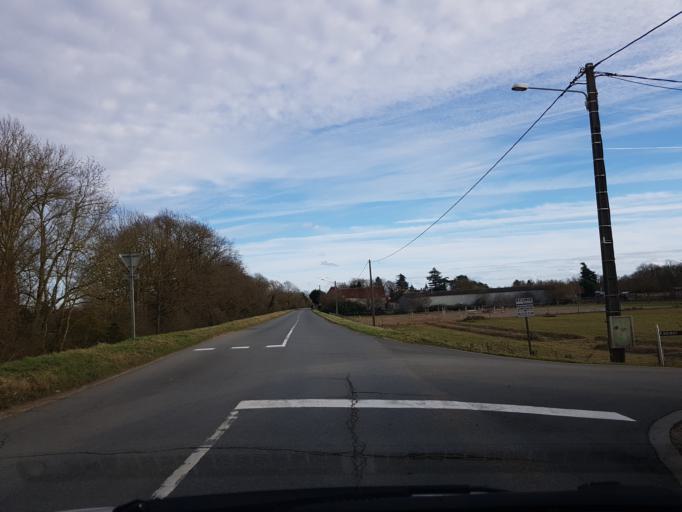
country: FR
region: Centre
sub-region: Departement du Loiret
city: Saint-Denis-en-Val
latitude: 47.8959
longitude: 1.9542
